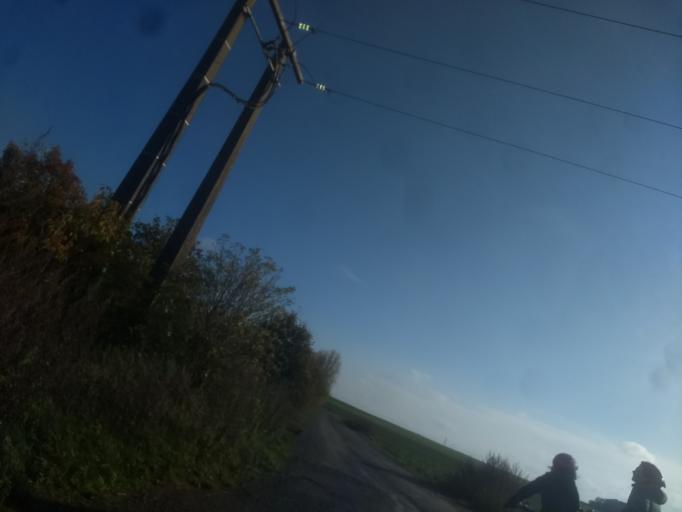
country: FR
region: Nord-Pas-de-Calais
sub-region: Departement du Pas-de-Calais
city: Tilloy-les-Mofflaines
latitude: 50.2741
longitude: 2.8054
